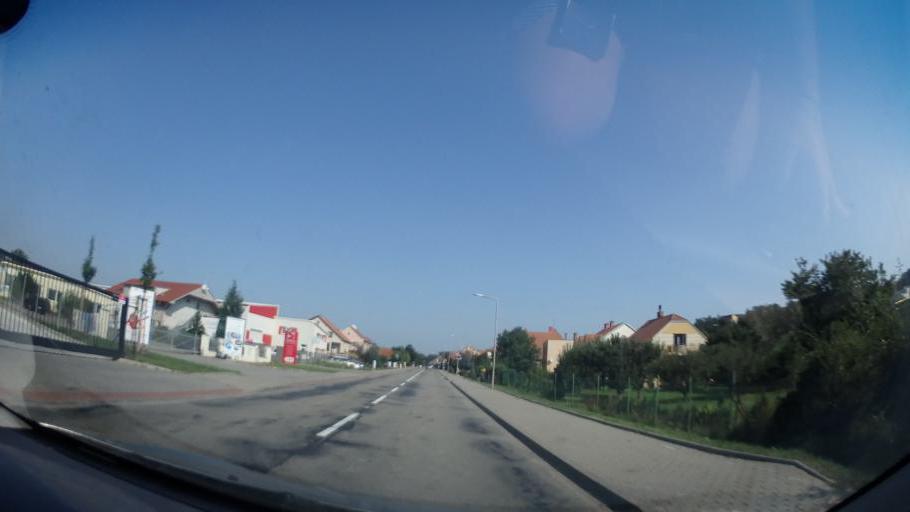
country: CZ
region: South Moravian
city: Kurim
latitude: 49.2634
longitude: 16.5273
